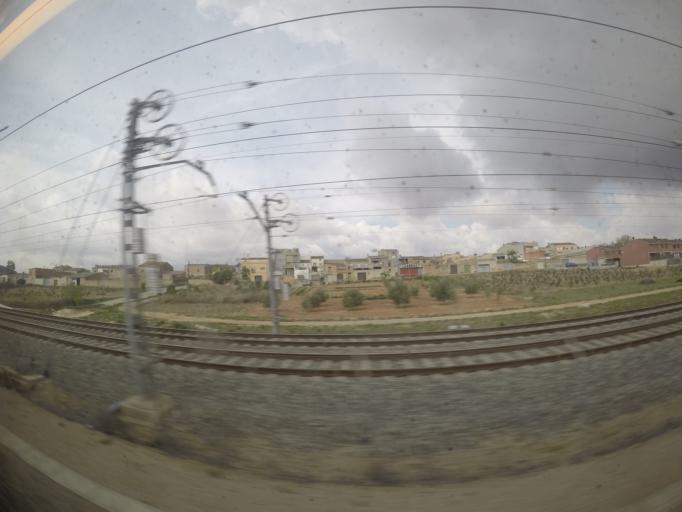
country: ES
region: Catalonia
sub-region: Provincia de Barcelona
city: Castellet
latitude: 41.2855
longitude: 1.6140
